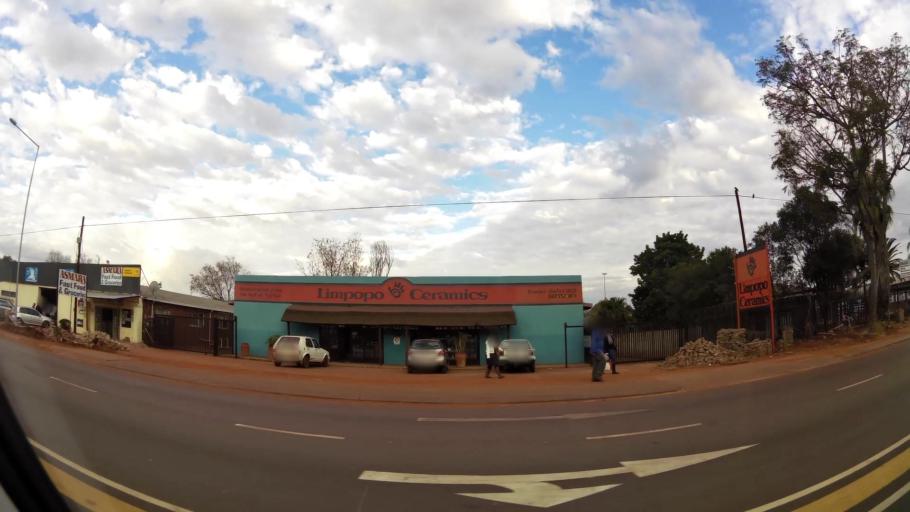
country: ZA
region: Limpopo
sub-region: Waterberg District Municipality
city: Modimolle
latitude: -24.5160
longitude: 28.7179
